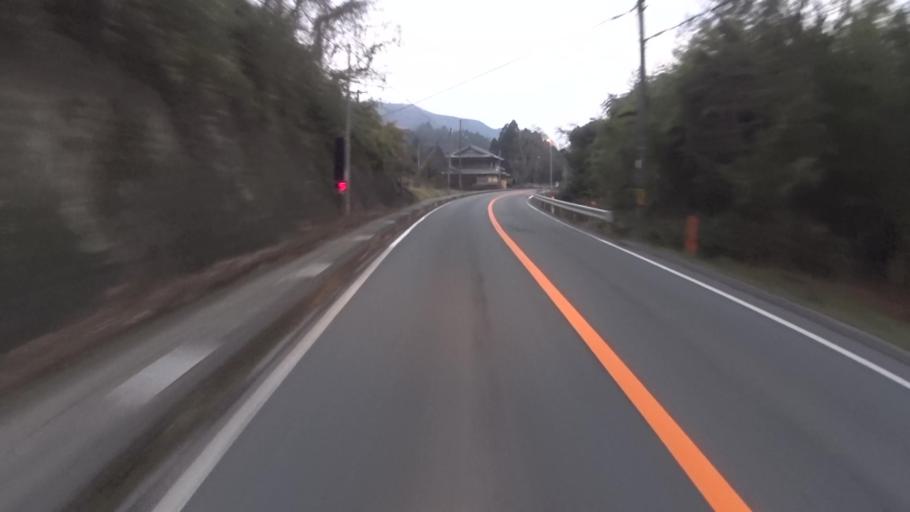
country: JP
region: Kyoto
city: Ayabe
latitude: 35.2972
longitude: 135.3279
